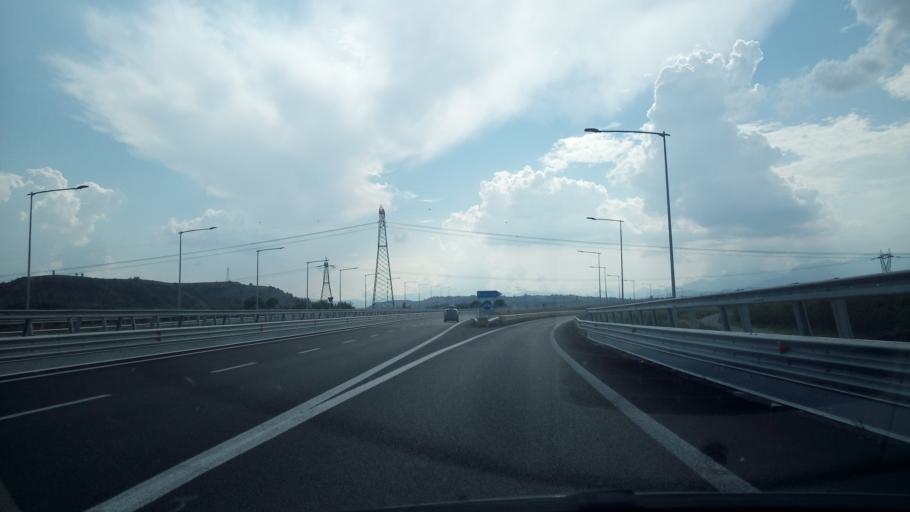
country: IT
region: Calabria
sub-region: Provincia di Cosenza
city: Doria
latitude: 39.7254
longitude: 16.3223
